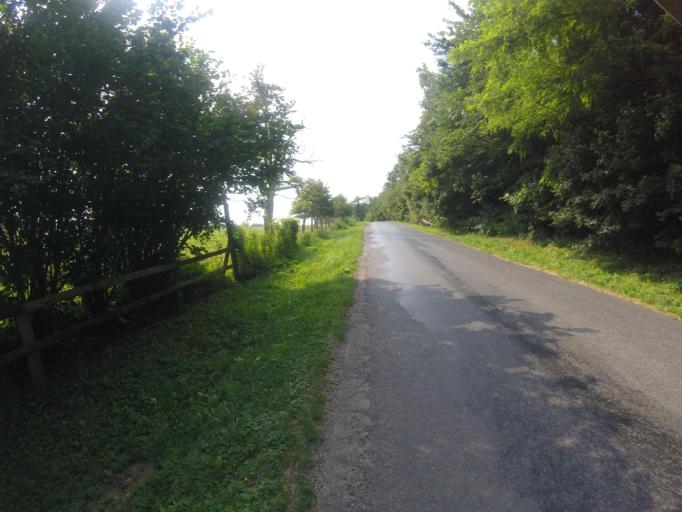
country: HU
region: Veszprem
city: Badacsonytomaj
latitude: 46.8323
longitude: 17.5118
